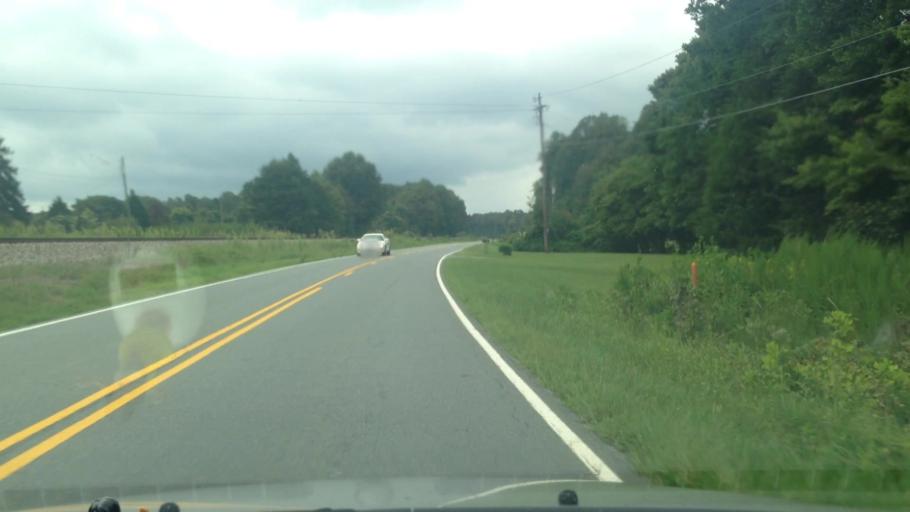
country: US
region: North Carolina
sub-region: Stokes County
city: Walnut Cove
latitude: 36.2548
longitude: -80.1483
